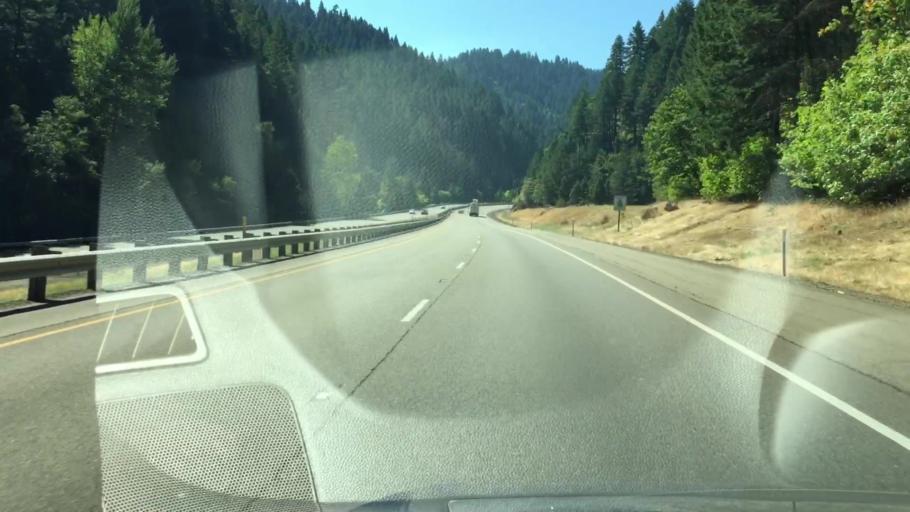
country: US
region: Oregon
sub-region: Douglas County
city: Canyonville
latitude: 42.8659
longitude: -123.2469
